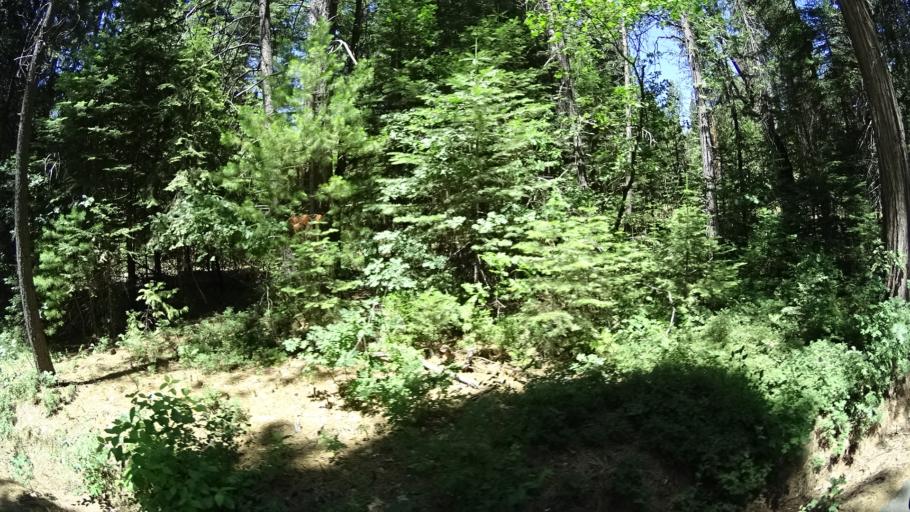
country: US
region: California
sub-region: Calaveras County
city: Arnold
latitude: 38.2441
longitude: -120.3097
